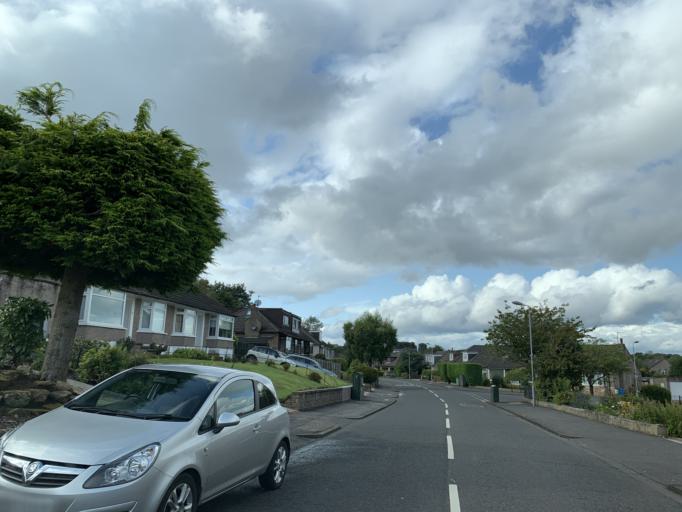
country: GB
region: Scotland
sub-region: East Renfrewshire
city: Newton Mearns
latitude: 55.7816
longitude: -4.3250
